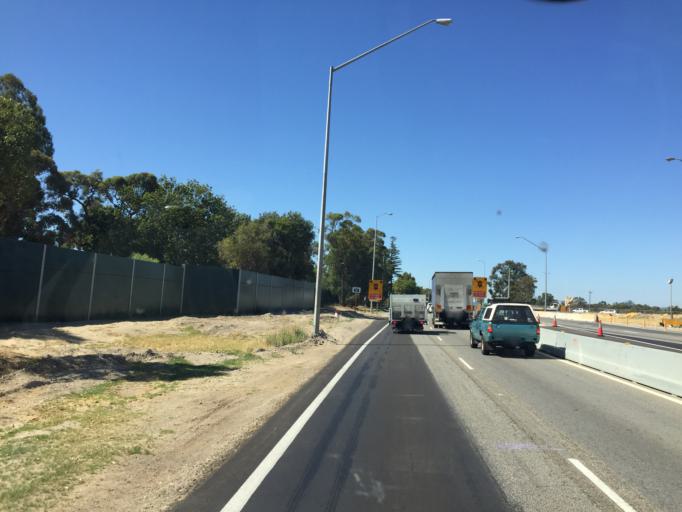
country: AU
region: Western Australia
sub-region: Kalamunda
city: Maida Vale
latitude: -31.9425
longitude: 116.0154
